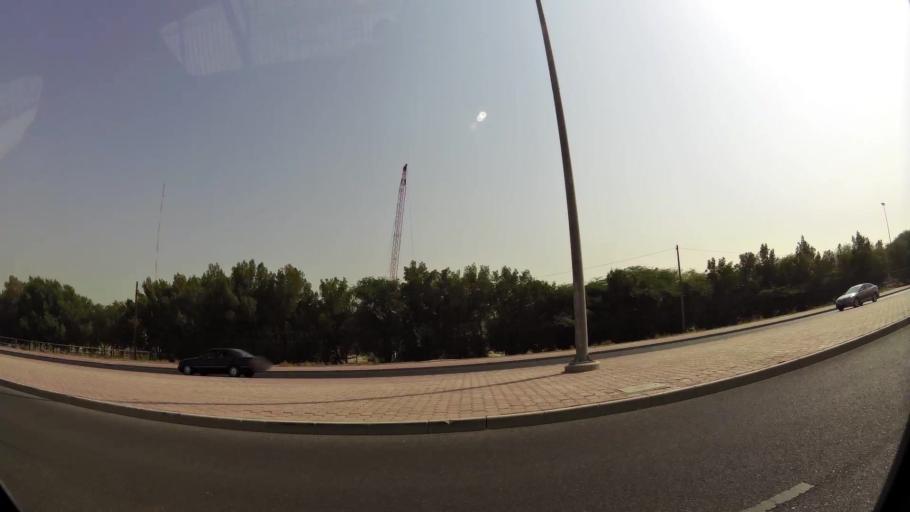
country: KW
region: Al Asimah
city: Ar Rabiyah
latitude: 29.2867
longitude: 47.9143
